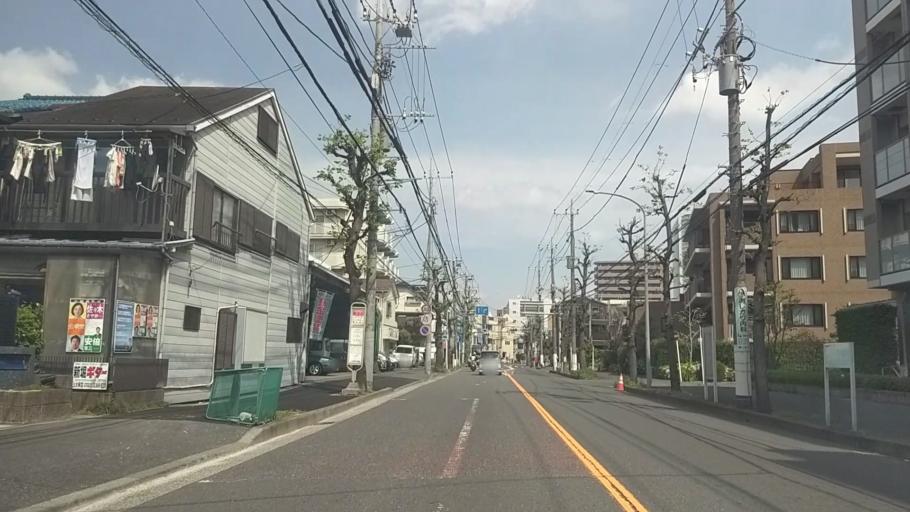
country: JP
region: Kanagawa
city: Yokohama
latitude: 35.4018
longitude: 139.5952
